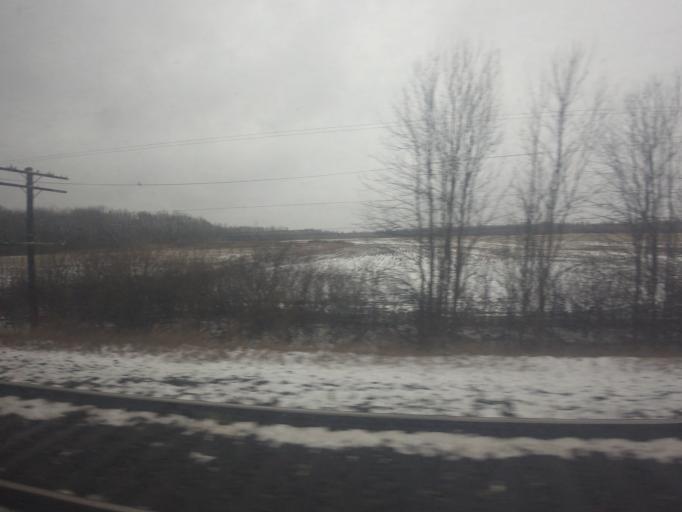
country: CA
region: Ontario
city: Quinte West
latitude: 44.1427
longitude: -77.5108
